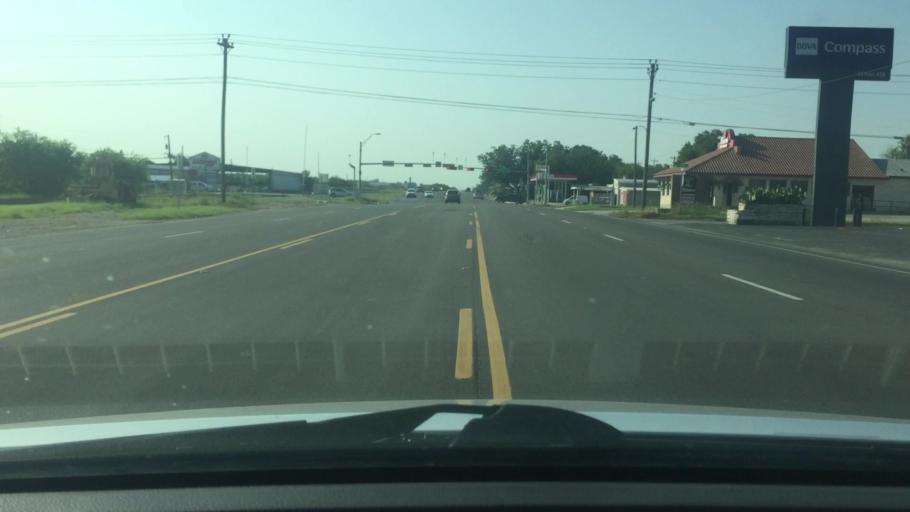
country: US
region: Texas
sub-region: Williamson County
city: Leander
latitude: 30.5800
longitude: -97.8535
